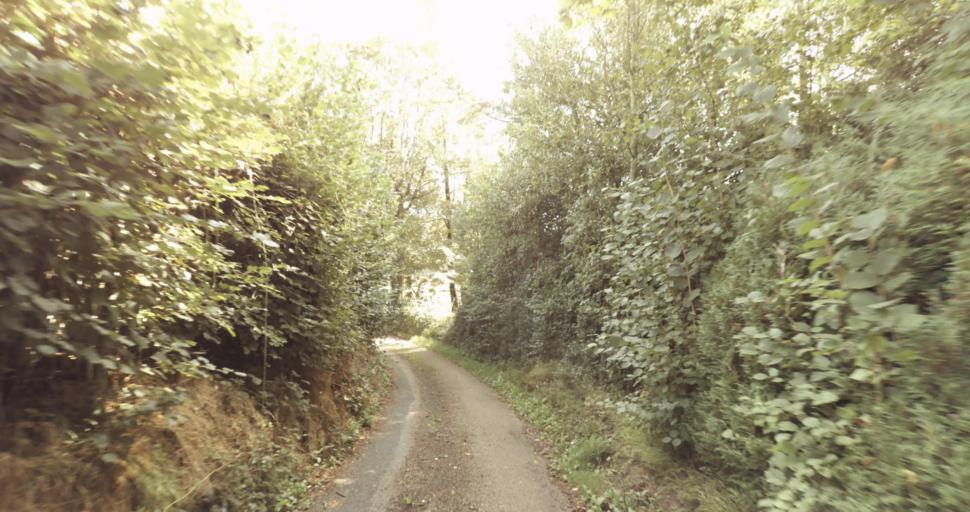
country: FR
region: Lower Normandy
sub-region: Departement de l'Orne
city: Gace
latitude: 48.7827
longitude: 0.3339
